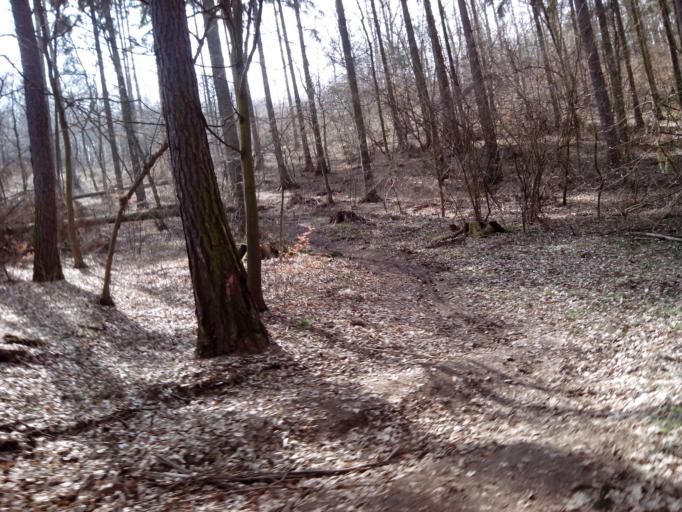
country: CZ
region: Central Bohemia
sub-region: Okres Beroun
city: Beroun
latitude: 49.9429
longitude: 14.1015
